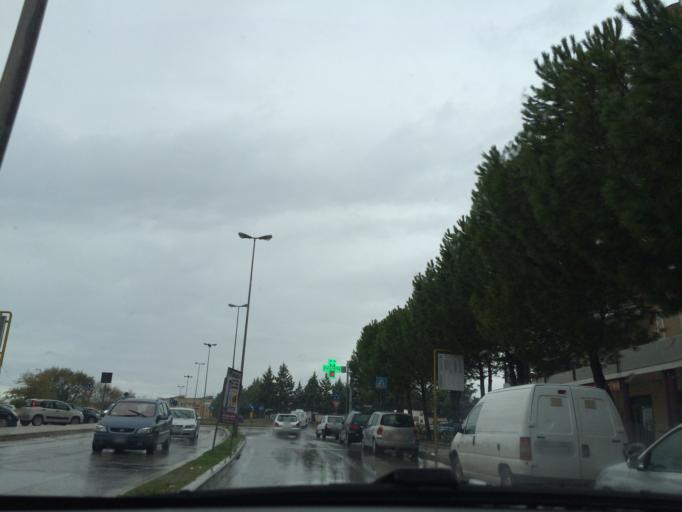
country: IT
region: Basilicate
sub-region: Provincia di Matera
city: Matera
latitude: 40.6787
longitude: 16.5812
